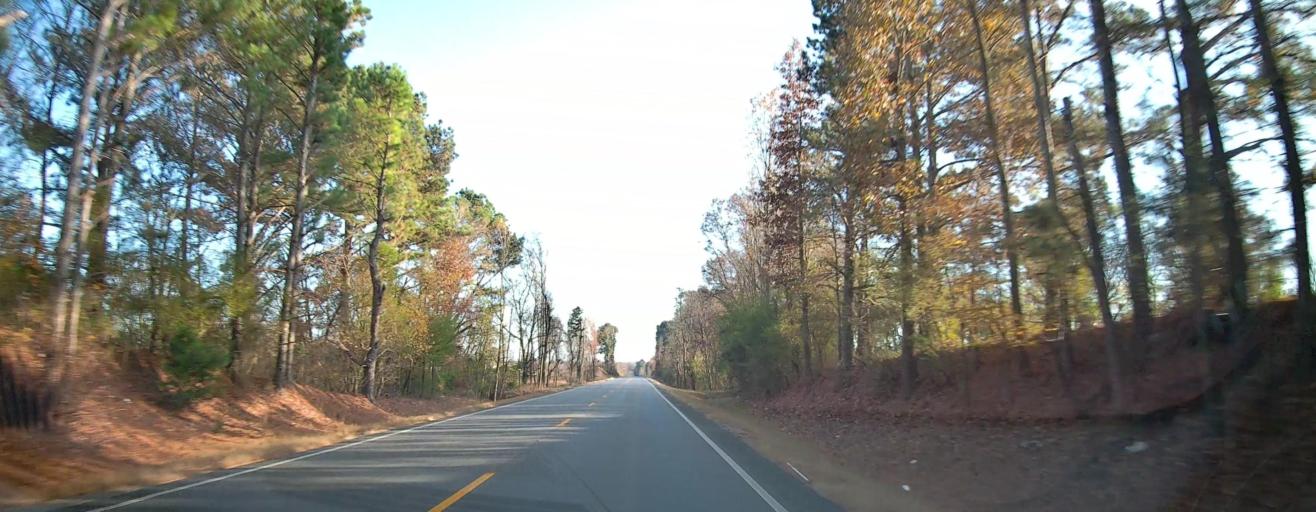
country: US
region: Alabama
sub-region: Marshall County
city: Arab
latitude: 34.2584
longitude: -86.5721
